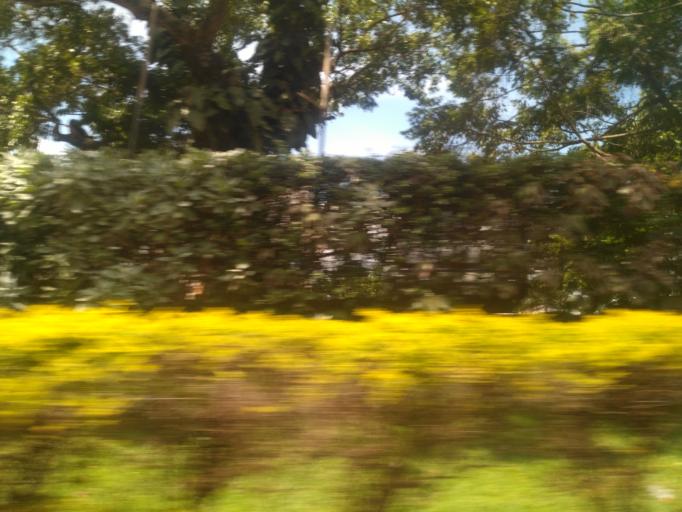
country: UG
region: Central Region
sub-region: Wakiso District
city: Entebbe
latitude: 0.0557
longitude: 32.4682
